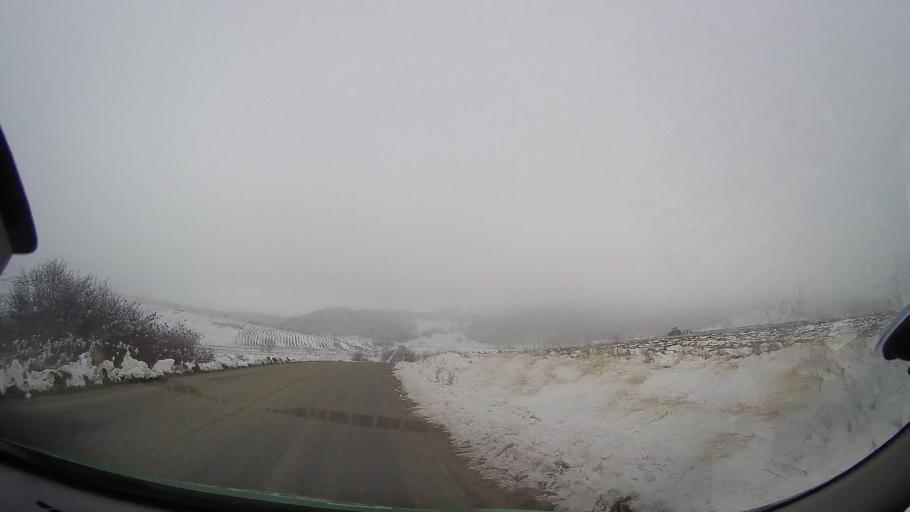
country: RO
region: Bacau
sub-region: Comuna Glavanesti
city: Frumuselu
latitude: 46.2678
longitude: 27.3131
